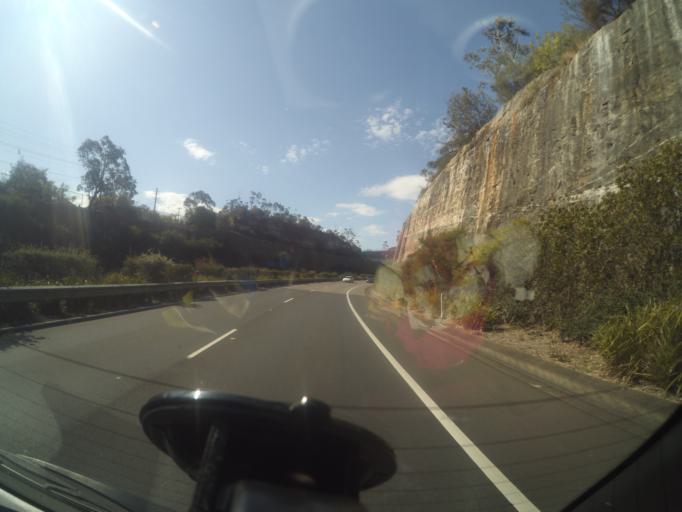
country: AU
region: New South Wales
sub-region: Blue Mountains Municipality
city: Hazelbrook
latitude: -33.7343
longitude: 150.4833
